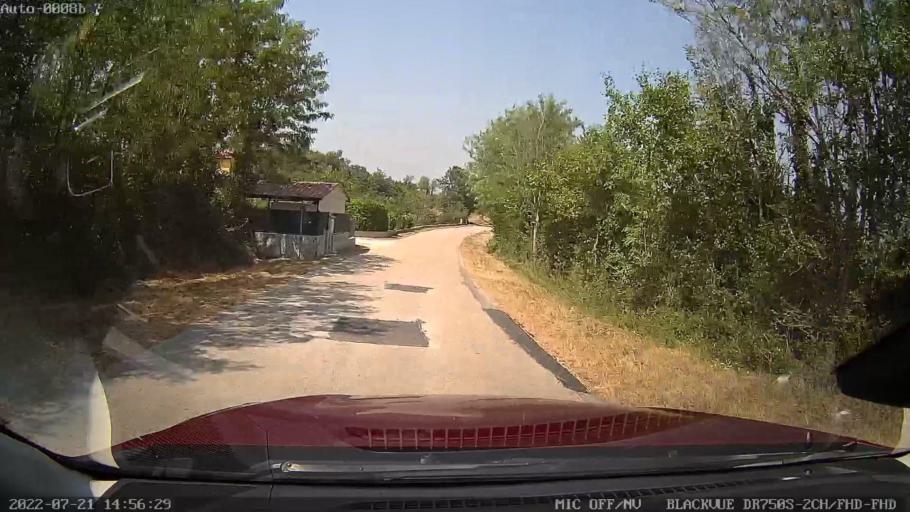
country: HR
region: Istarska
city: Pazin
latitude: 45.2011
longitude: 13.9487
